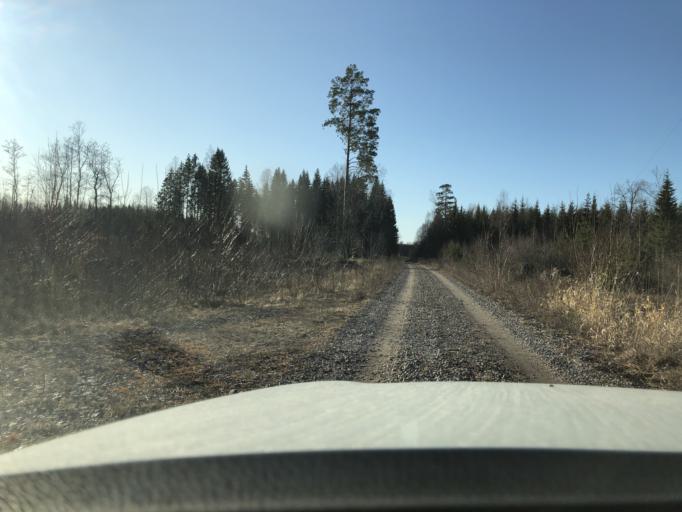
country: SE
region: Gaevleborg
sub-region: Gavle Kommun
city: Hedesunda
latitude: 60.2992
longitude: 16.8893
